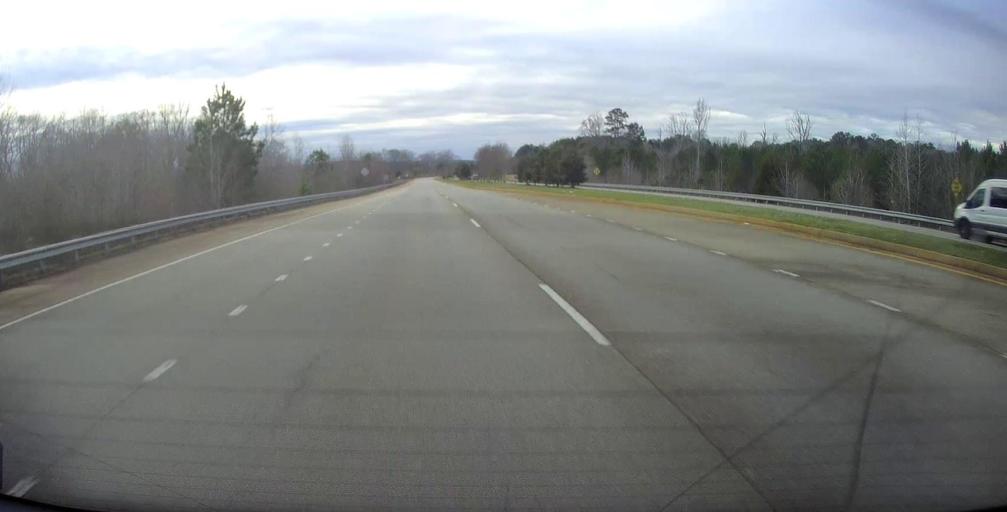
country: US
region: Georgia
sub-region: Troup County
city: West Point
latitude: 32.9310
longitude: -85.1203
